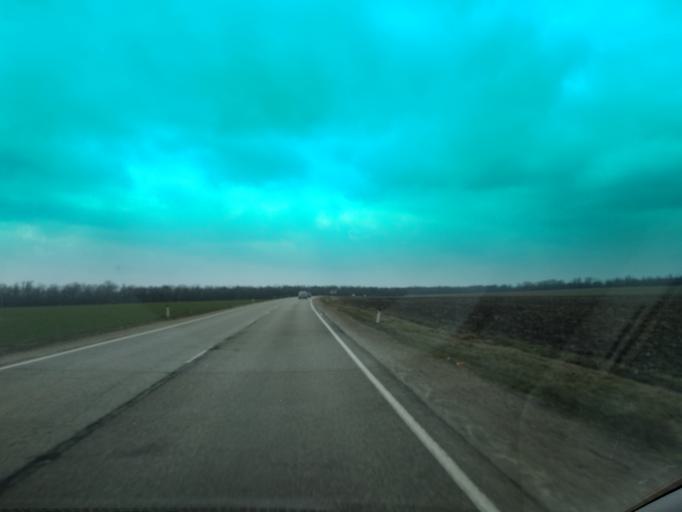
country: RU
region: Krasnodarskiy
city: Novomalorossiyskaya
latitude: 45.7324
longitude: 39.9081
